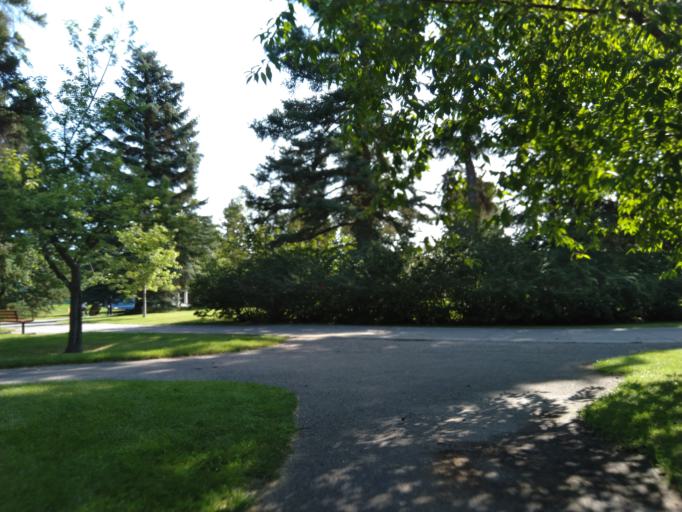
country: CA
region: Alberta
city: Calgary
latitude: 51.1007
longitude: -114.2218
